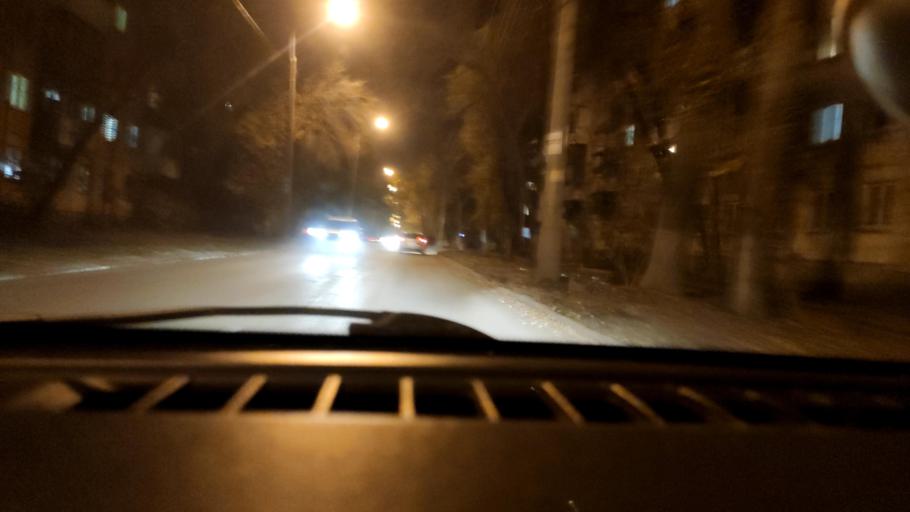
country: RU
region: Samara
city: Samara
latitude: 53.1931
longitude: 50.1839
